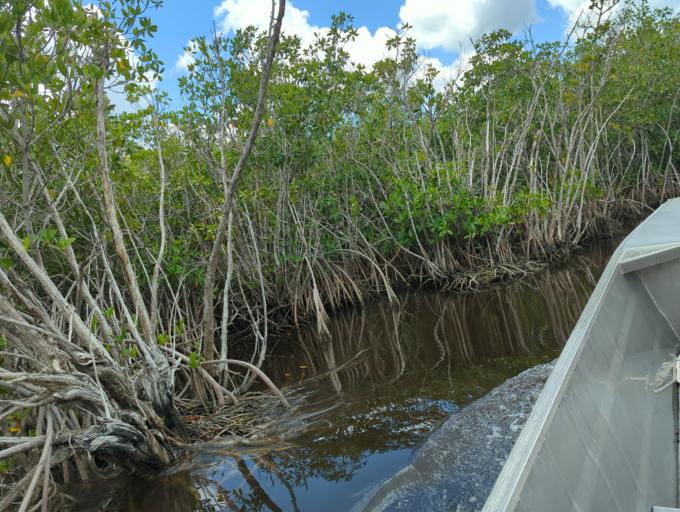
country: US
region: Florida
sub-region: Collier County
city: Marco
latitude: 25.9047
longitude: -81.3739
